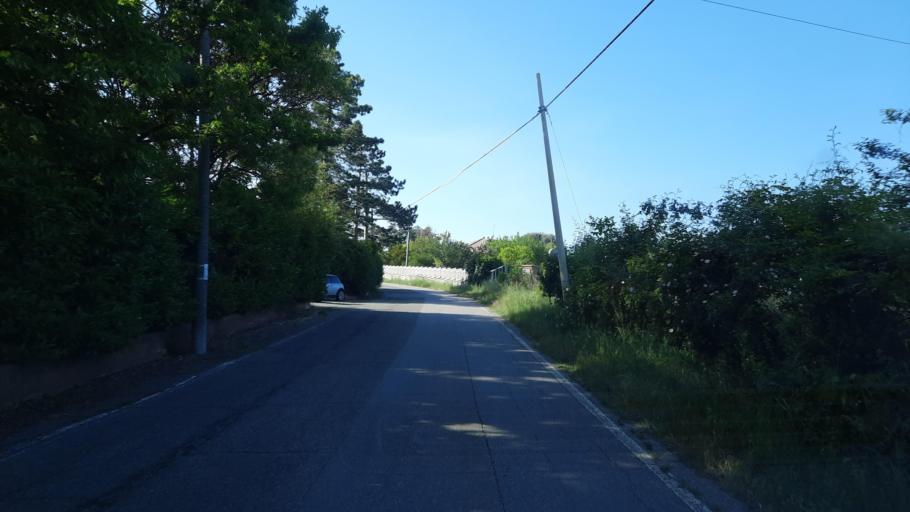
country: IT
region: Piedmont
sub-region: Provincia di Alessandria
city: San Giorgio
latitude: 45.1124
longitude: 8.4098
